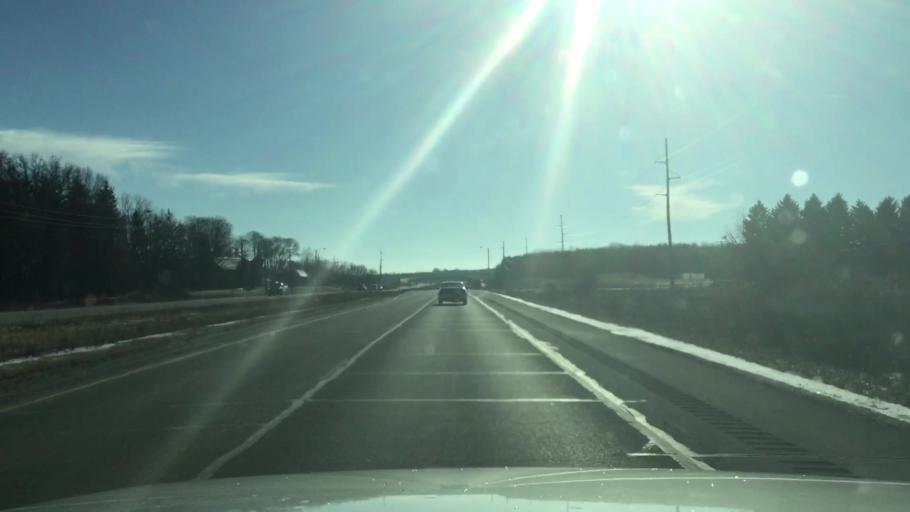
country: US
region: Wisconsin
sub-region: Racine County
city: Rochester
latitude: 42.7284
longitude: -88.2213
